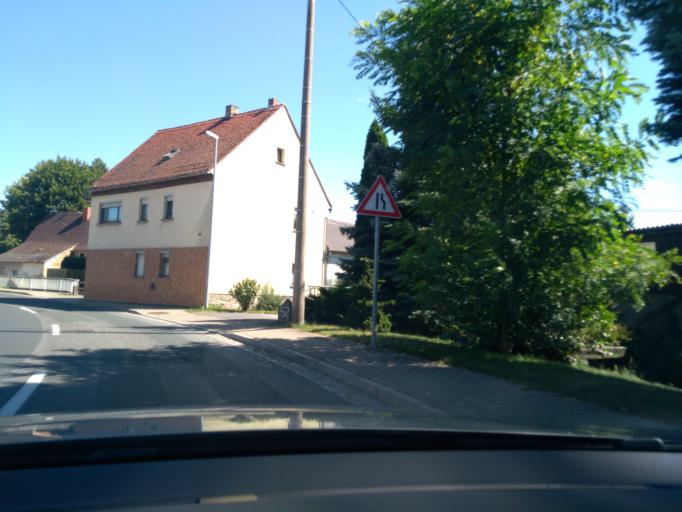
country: DE
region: Saxony
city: Grossrohrsdorf
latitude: 51.1422
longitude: 14.0382
